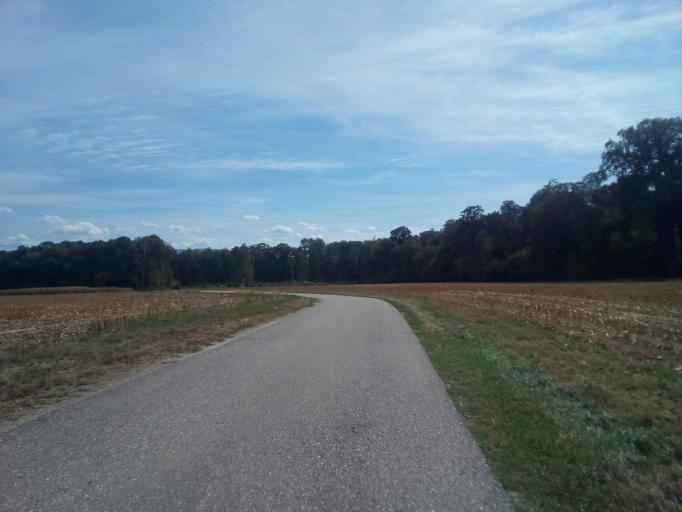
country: DE
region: Baden-Wuerttemberg
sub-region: Karlsruhe Region
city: Lichtenau
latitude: 48.7041
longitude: 8.0141
